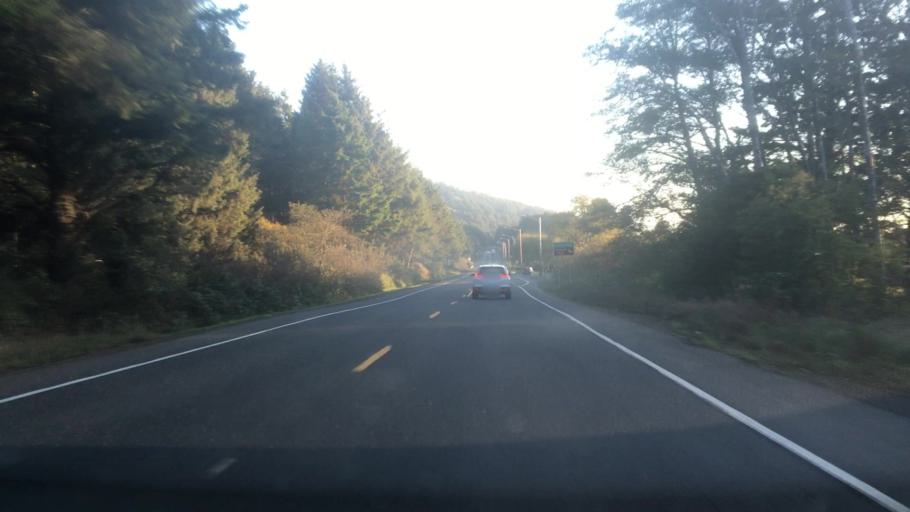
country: US
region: Oregon
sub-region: Clatsop County
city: Cannon Beach
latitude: 45.8754
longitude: -123.9579
